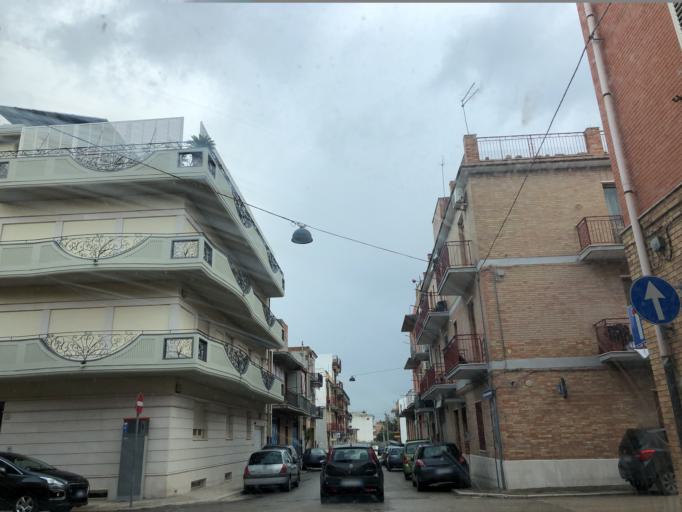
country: IT
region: Apulia
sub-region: Provincia di Foggia
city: Lucera
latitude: 41.5033
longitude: 15.3410
